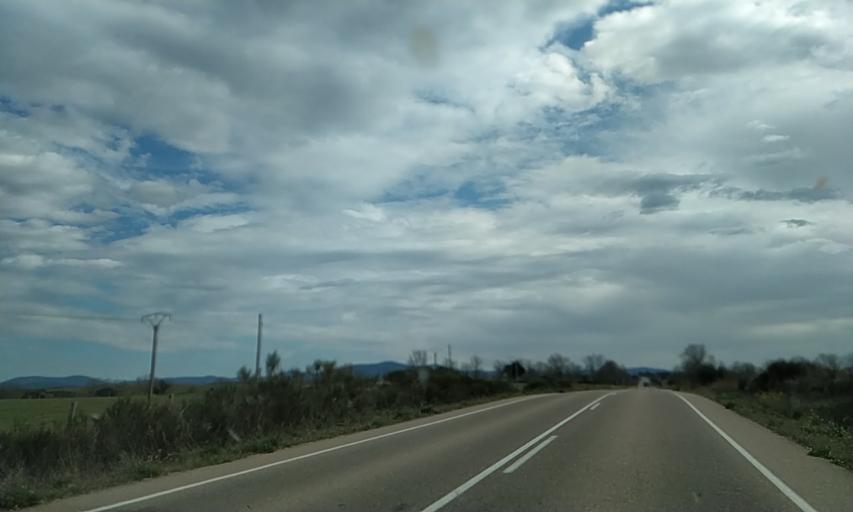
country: ES
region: Castille and Leon
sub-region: Provincia de Salamanca
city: Robleda
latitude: 40.4081
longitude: -6.6038
